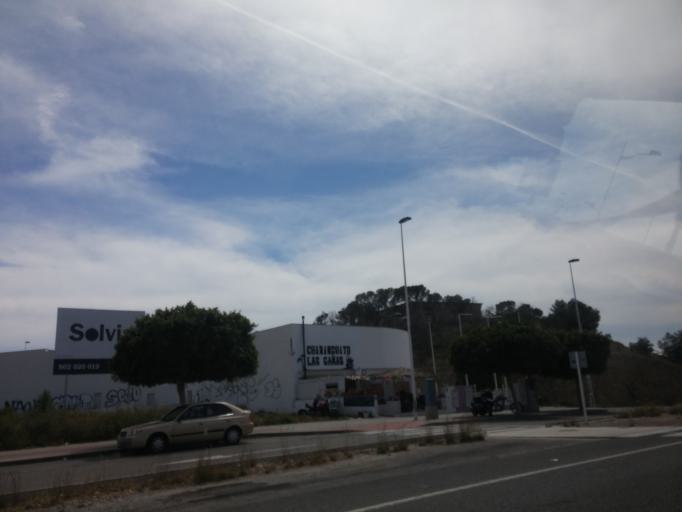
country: ES
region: Valencia
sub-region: Provincia de Alicante
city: Villajoyosa
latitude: 38.5017
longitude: -0.2459
